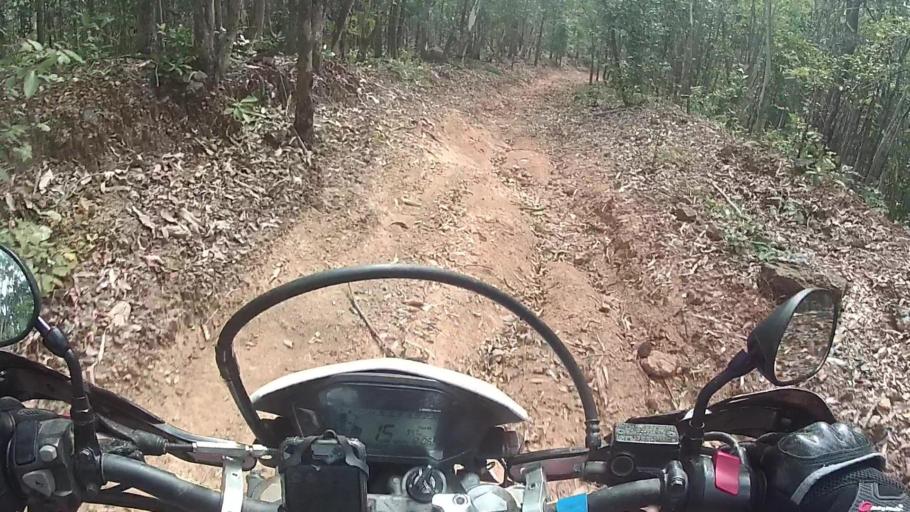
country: TH
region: Chiang Mai
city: Mae On
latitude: 18.7278
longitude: 99.2848
